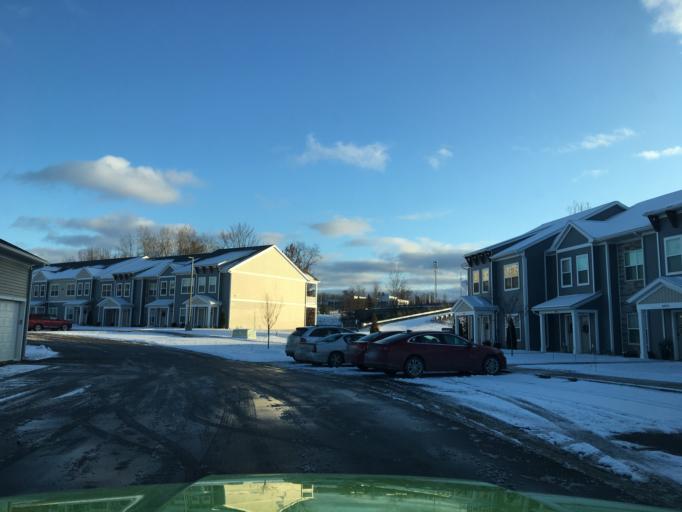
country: US
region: Michigan
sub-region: Kent County
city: Rockford
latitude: 43.1221
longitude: -85.6014
